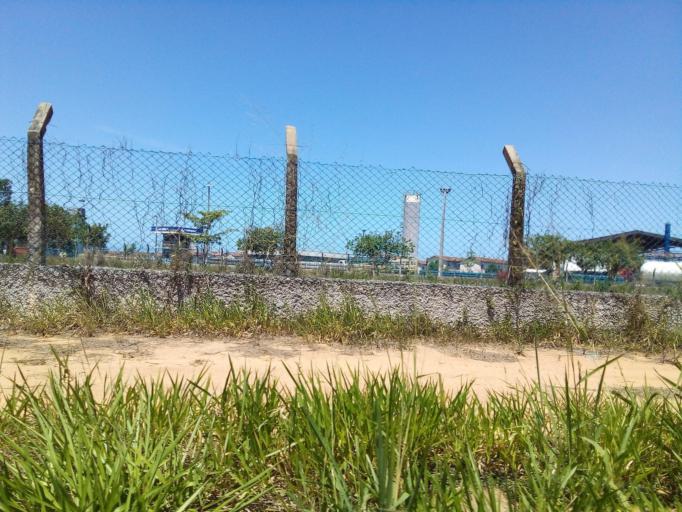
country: BR
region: Espirito Santo
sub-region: Aracruz
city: Aracruz
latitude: -19.8224
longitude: -40.0676
